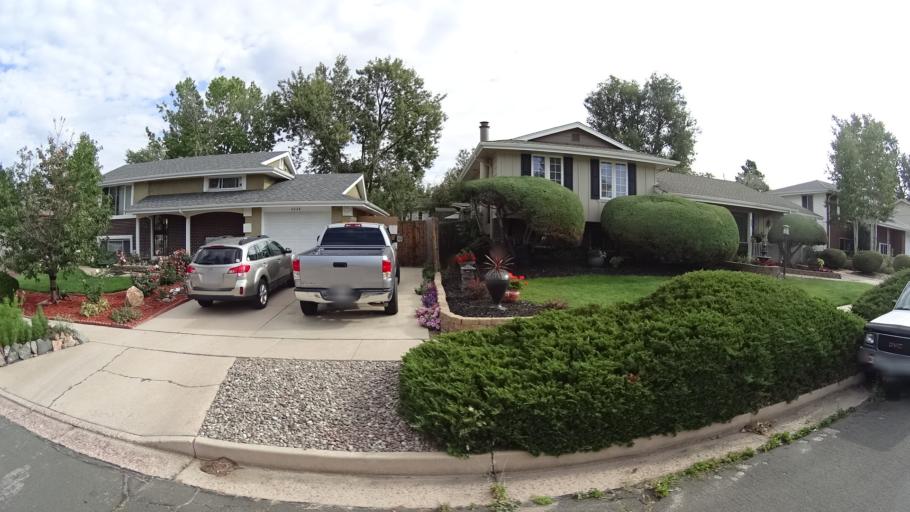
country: US
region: Colorado
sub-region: El Paso County
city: Cimarron Hills
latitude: 38.8446
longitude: -104.7522
